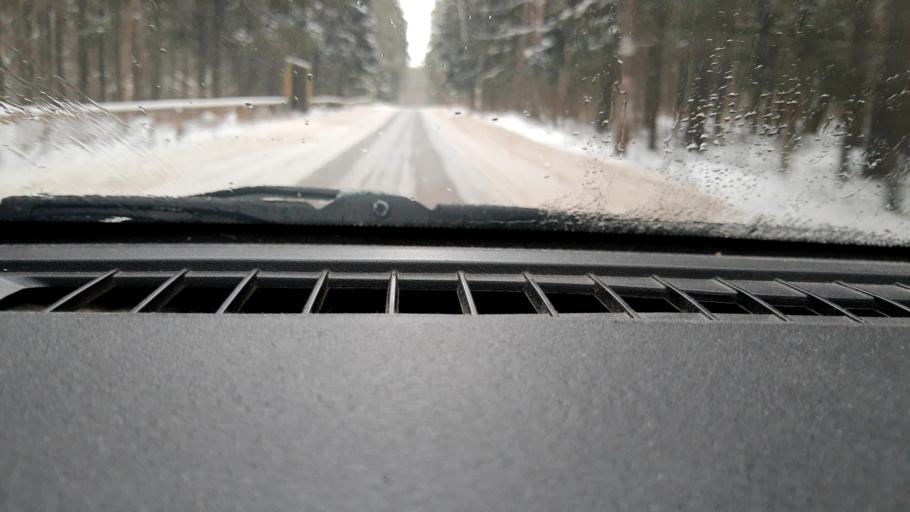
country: RU
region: Nizjnij Novgorod
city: Afonino
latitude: 56.1773
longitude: 44.0773
